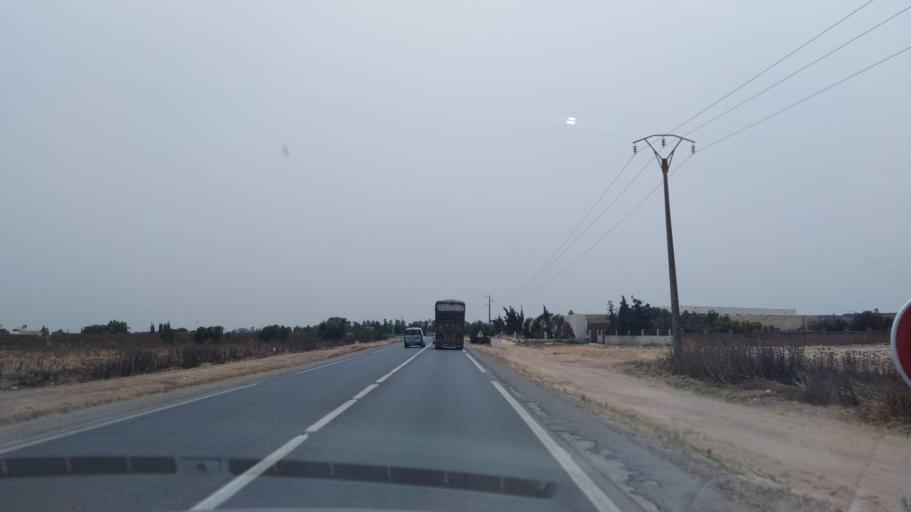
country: MA
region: Chaouia-Ouardigha
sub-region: Settat Province
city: Berrechid
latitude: 33.3217
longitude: -7.5733
